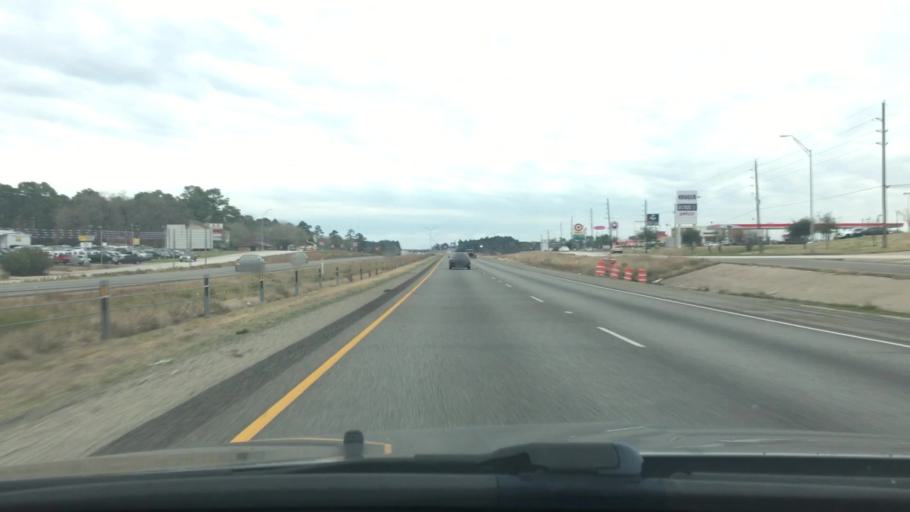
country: US
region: Texas
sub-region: Walker County
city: Huntsville
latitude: 30.7114
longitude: -95.5653
